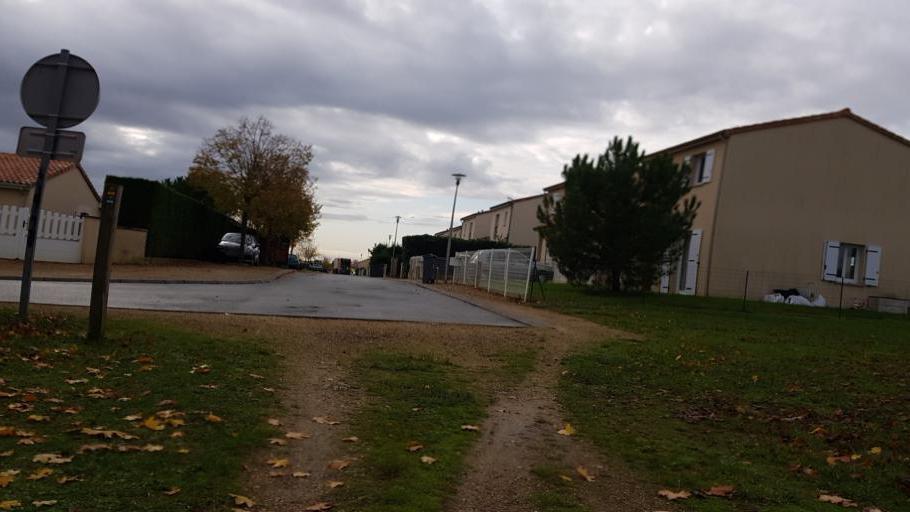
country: FR
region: Poitou-Charentes
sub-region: Departement de la Vienne
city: Chasseneuil-du-Poitou
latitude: 46.6454
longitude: 0.3572
